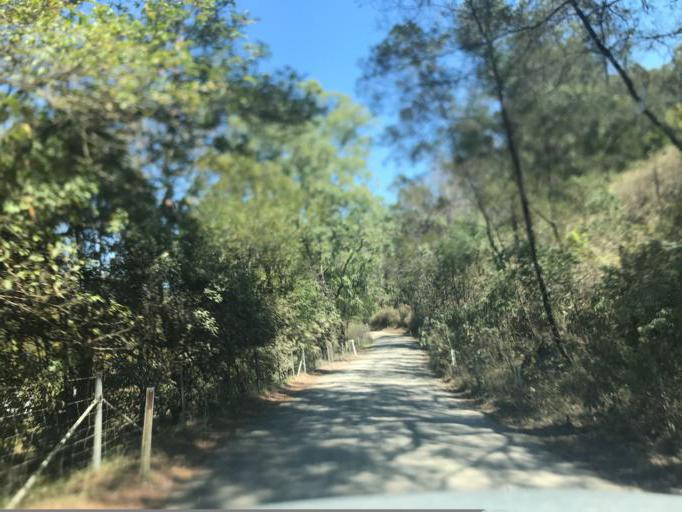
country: AU
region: New South Wales
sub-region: Hawkesbury
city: Pitt Town
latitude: -33.4237
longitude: 150.8949
